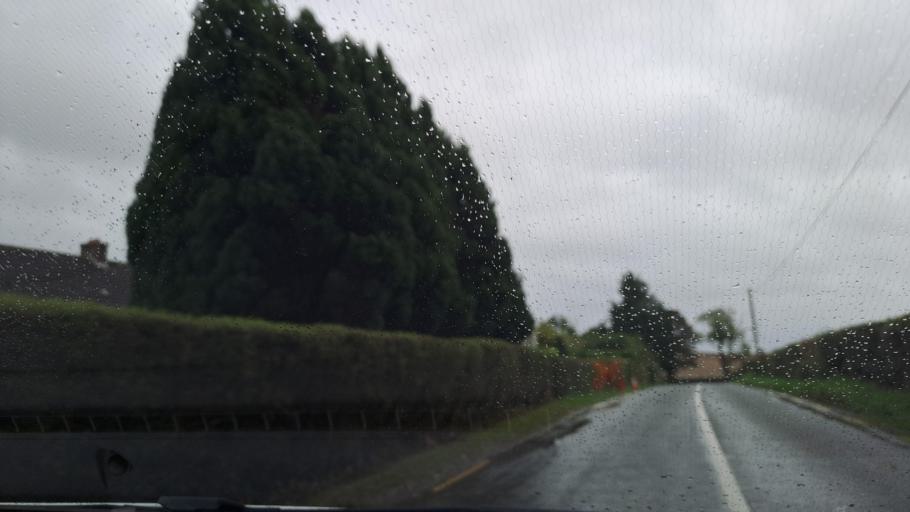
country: IE
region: Leinster
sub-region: Lu
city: Dundalk
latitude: 53.9646
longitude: -6.4660
